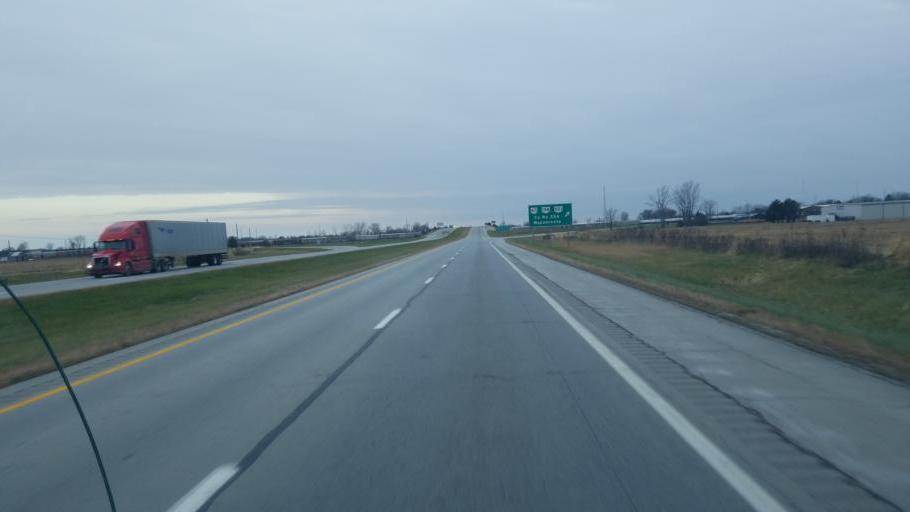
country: US
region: Ohio
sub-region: Auglaize County
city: Wapakoneta
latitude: 40.5558
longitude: -84.1848
